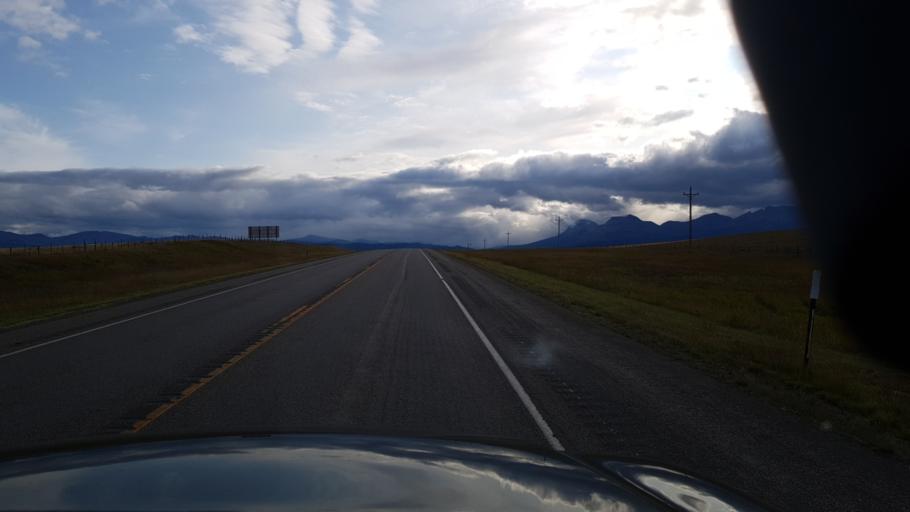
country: US
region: Montana
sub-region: Glacier County
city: South Browning
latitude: 48.4841
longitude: -113.1351
